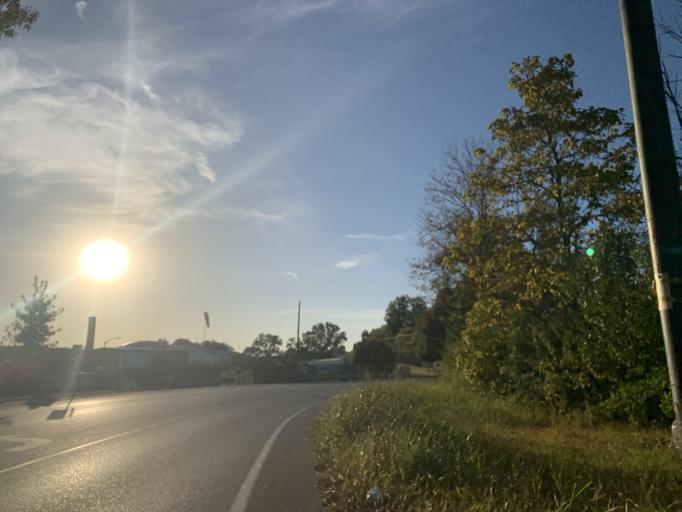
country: US
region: Kentucky
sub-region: Jefferson County
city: Shively
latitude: 38.2326
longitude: -85.8298
